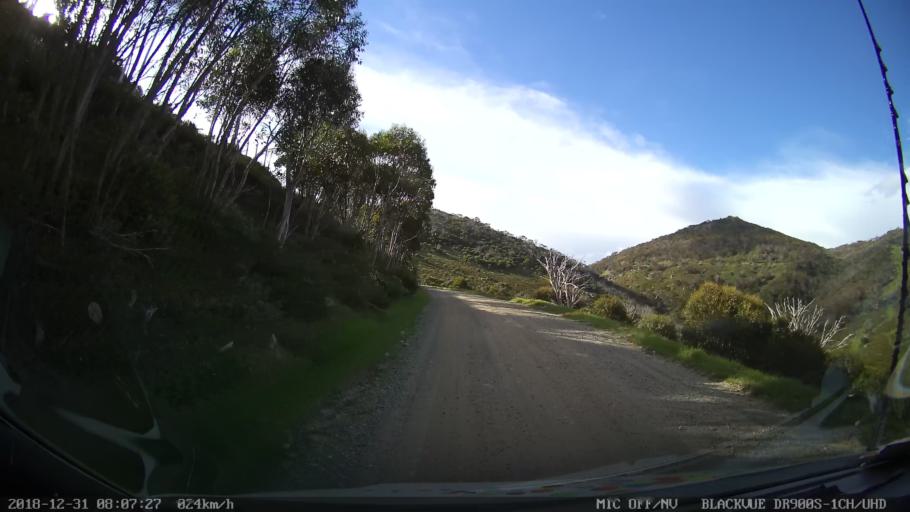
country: AU
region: New South Wales
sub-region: Snowy River
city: Jindabyne
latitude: -36.3790
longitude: 148.4092
